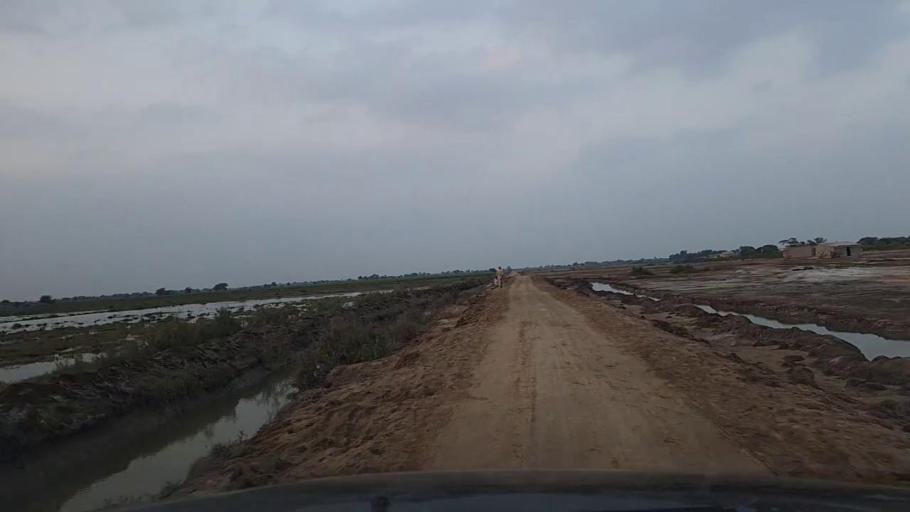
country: PK
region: Sindh
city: Jati
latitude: 24.4980
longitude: 68.3931
